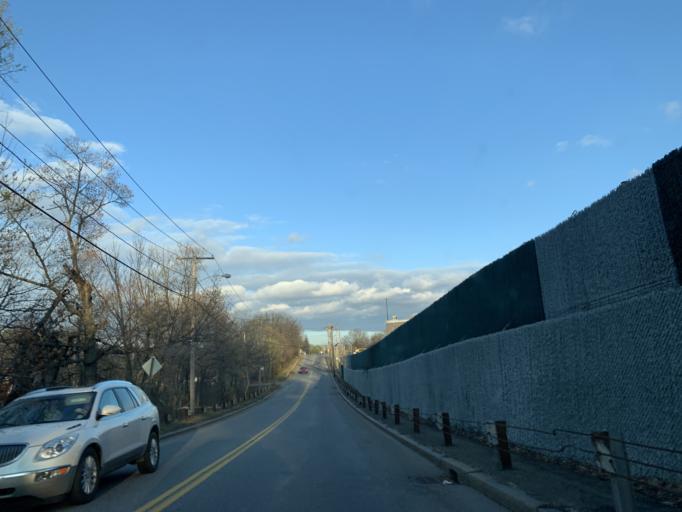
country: US
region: Rhode Island
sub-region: Providence County
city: Valley Falls
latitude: 41.8978
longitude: -71.3762
